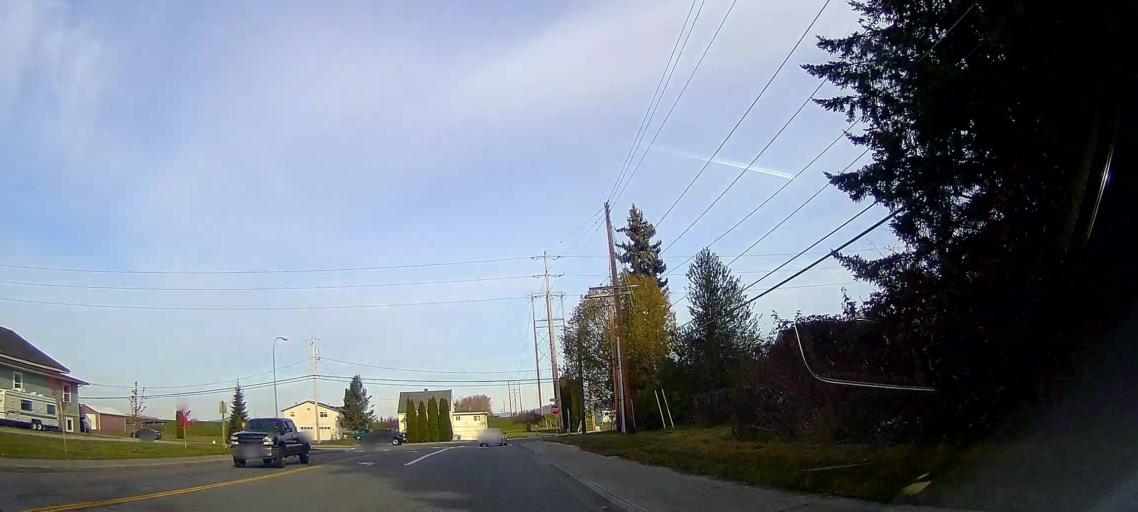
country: US
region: Washington
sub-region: Skagit County
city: Mount Vernon
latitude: 48.4425
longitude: -122.3321
